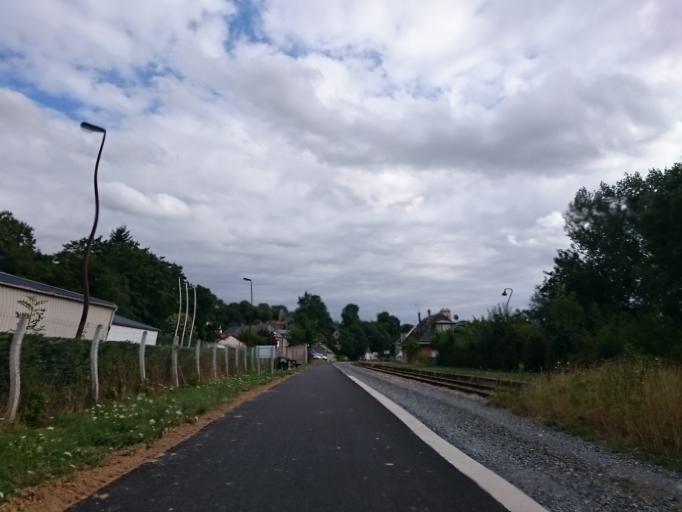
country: FR
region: Lower Normandy
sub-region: Departement du Calvados
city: Thury-Harcourt
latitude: 48.9908
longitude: -0.4819
